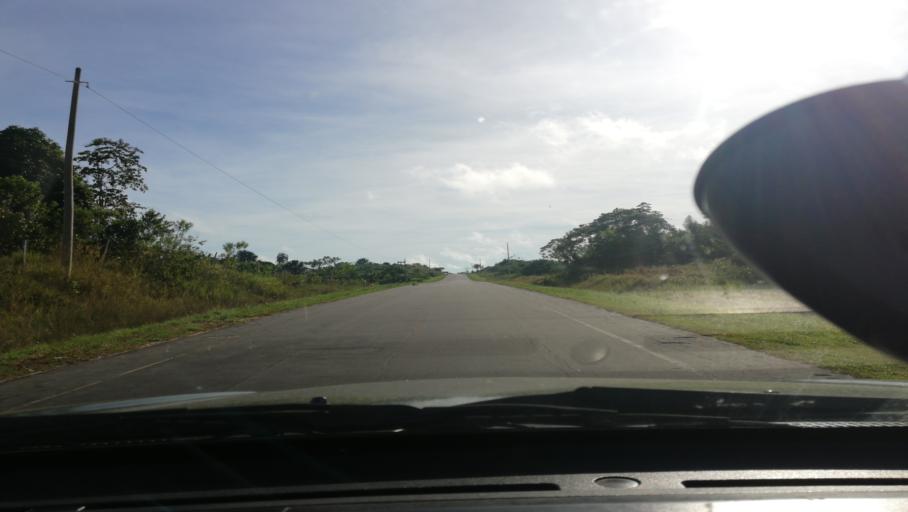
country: PE
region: Loreto
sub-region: Provincia de Loreto
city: Nauta
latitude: -4.3495
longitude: -73.5445
